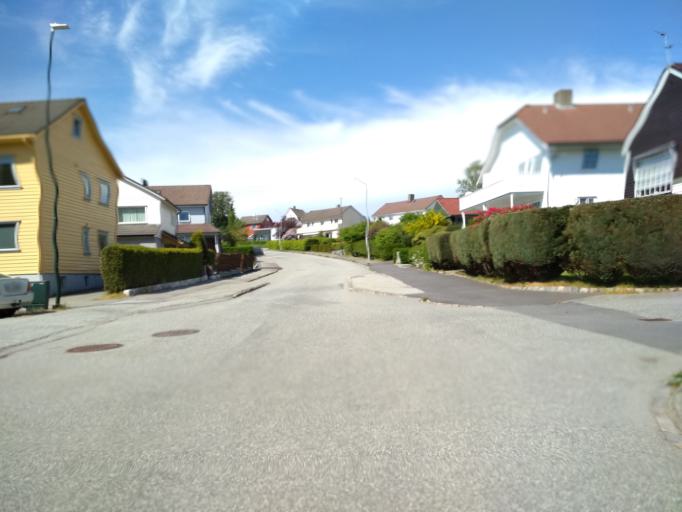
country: NO
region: Rogaland
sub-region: Stavanger
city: Stavanger
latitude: 58.9551
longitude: 5.7343
